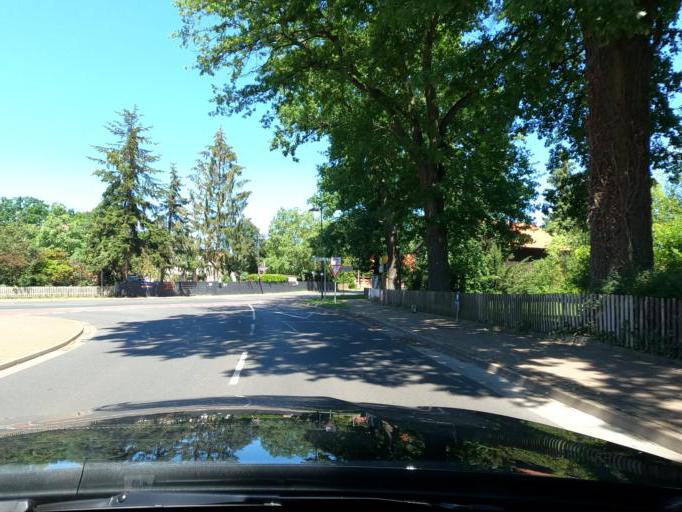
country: DE
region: Lower Saxony
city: Wathlingen
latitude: 52.5387
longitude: 10.1575
